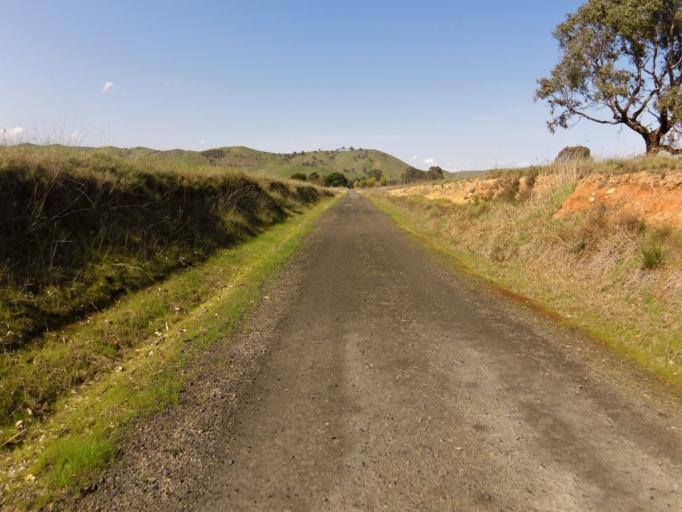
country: AU
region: Victoria
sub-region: Murrindindi
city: Alexandra
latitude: -37.0148
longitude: 145.7856
